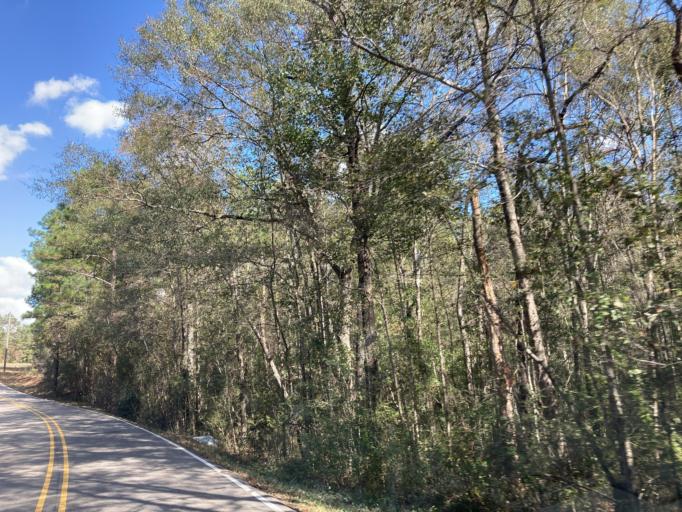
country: US
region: Mississippi
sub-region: Lamar County
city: West Hattiesburg
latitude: 31.2671
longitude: -89.3841
